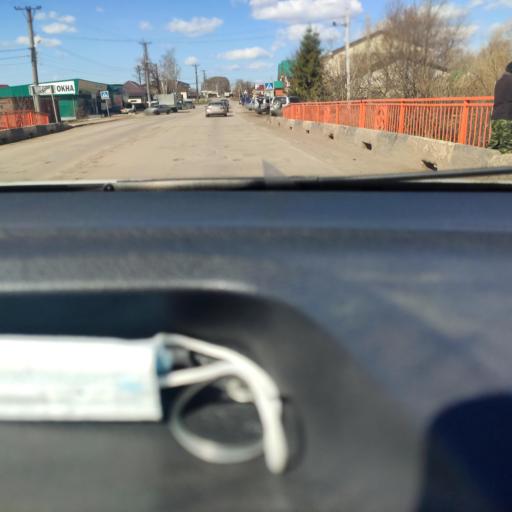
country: RU
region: Bashkortostan
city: Alekseyevka
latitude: 54.6914
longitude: 55.0123
